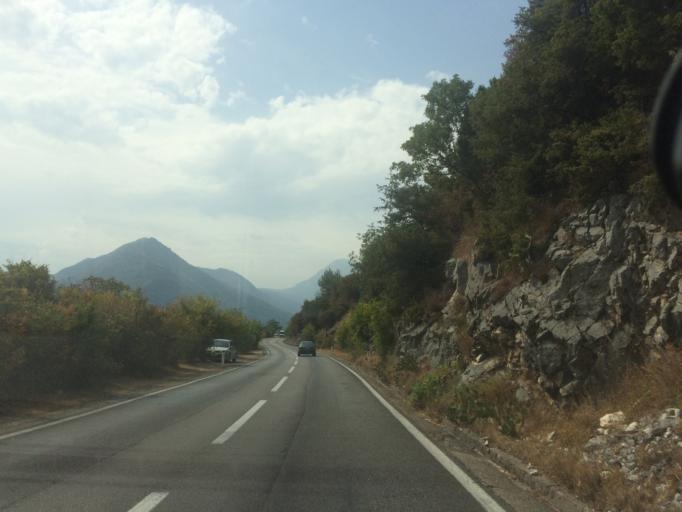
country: ME
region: Kotor
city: Risan
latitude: 42.4839
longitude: 18.7124
